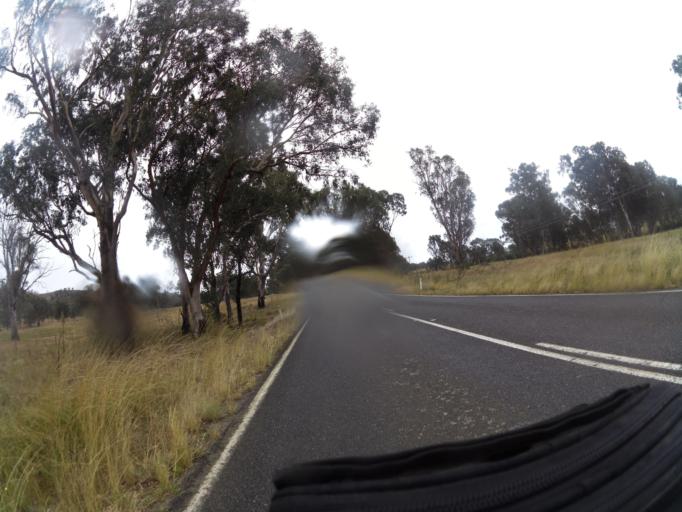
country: AU
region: New South Wales
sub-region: Greater Hume Shire
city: Holbrook
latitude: -36.2083
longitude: 147.8084
